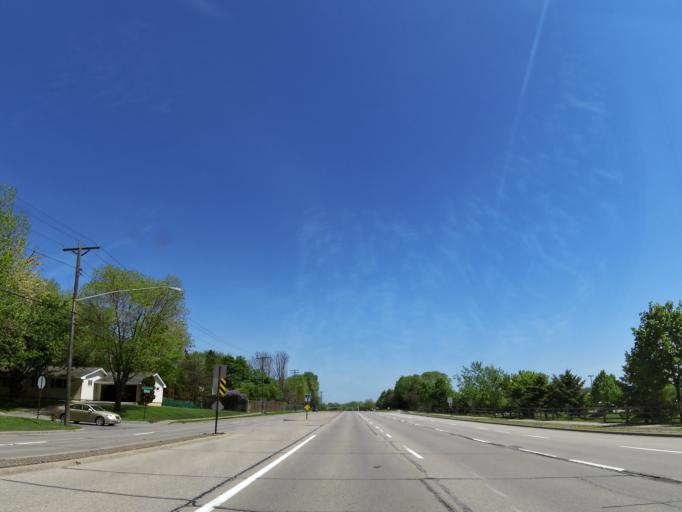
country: US
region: Minnesota
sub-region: Scott County
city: Savage
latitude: 44.8078
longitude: -93.3569
